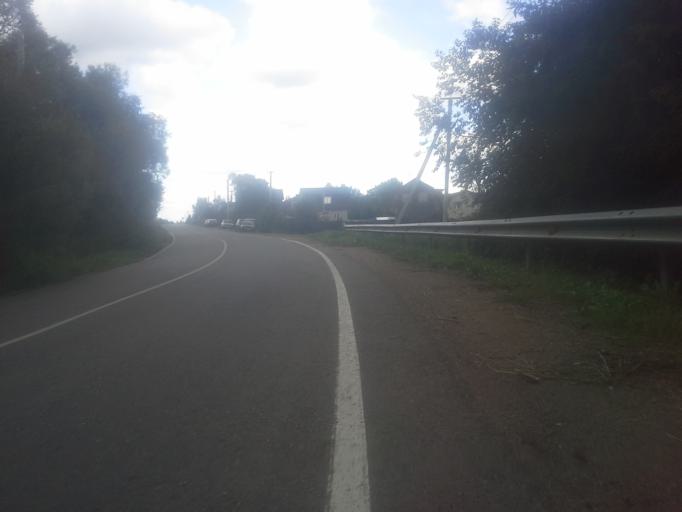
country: RU
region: Moskovskaya
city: Karinskoye
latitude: 55.6542
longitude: 36.6203
